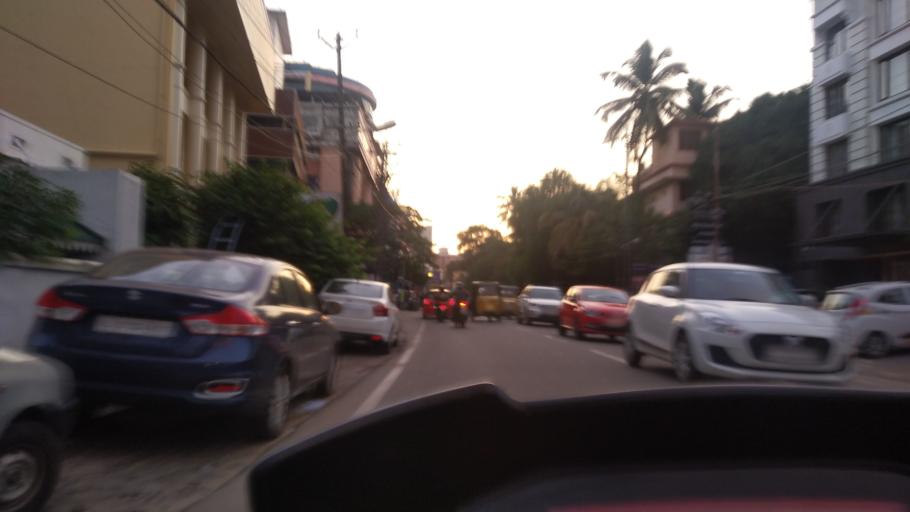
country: IN
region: Kerala
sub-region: Ernakulam
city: Cochin
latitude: 9.9788
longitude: 76.2864
